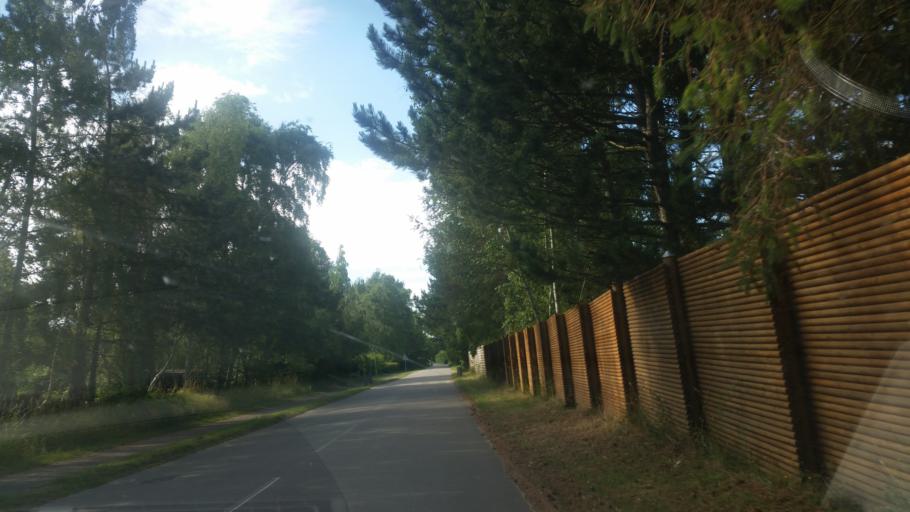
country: DK
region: Zealand
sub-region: Odsherred Kommune
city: Horve
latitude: 55.8240
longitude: 11.4017
